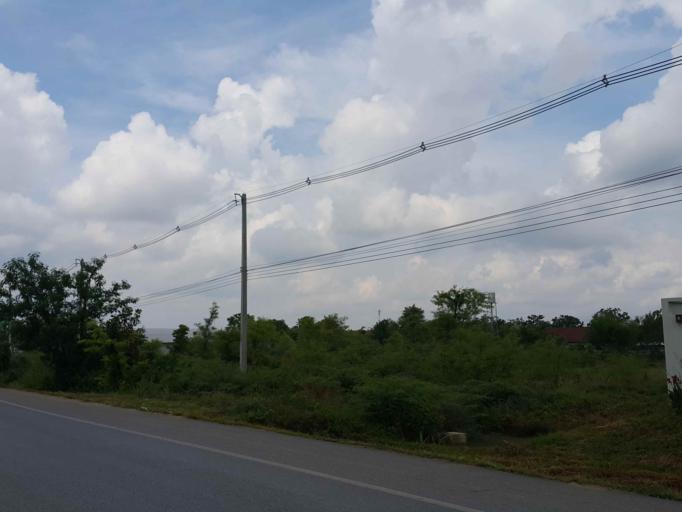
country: TH
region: Chiang Mai
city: Saraphi
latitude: 18.7608
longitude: 99.0642
